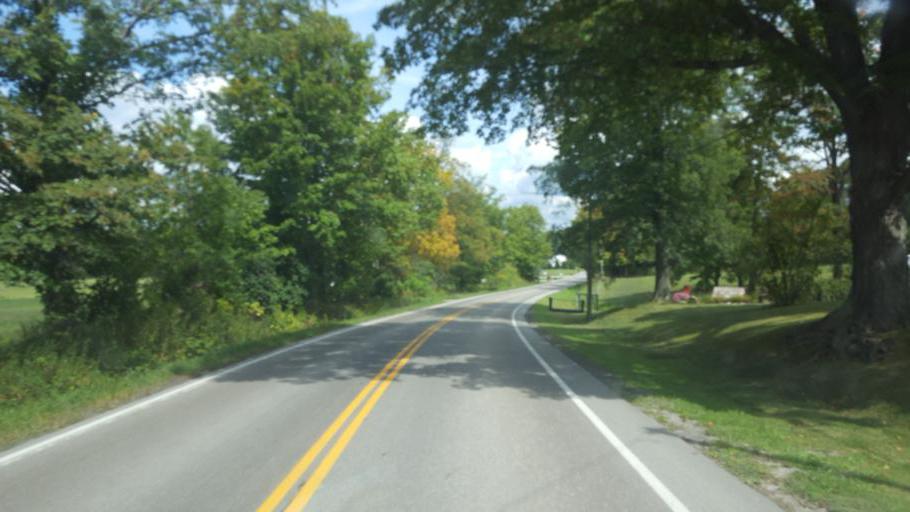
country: US
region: Ohio
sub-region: Geauga County
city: Middlefield
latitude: 41.4136
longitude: -81.1087
